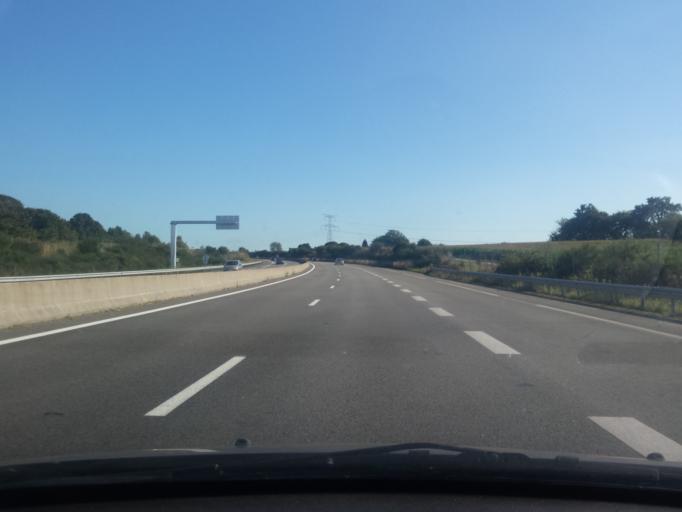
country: FR
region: Brittany
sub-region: Departement du Morbihan
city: Colpo
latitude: 47.7772
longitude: -2.7980
